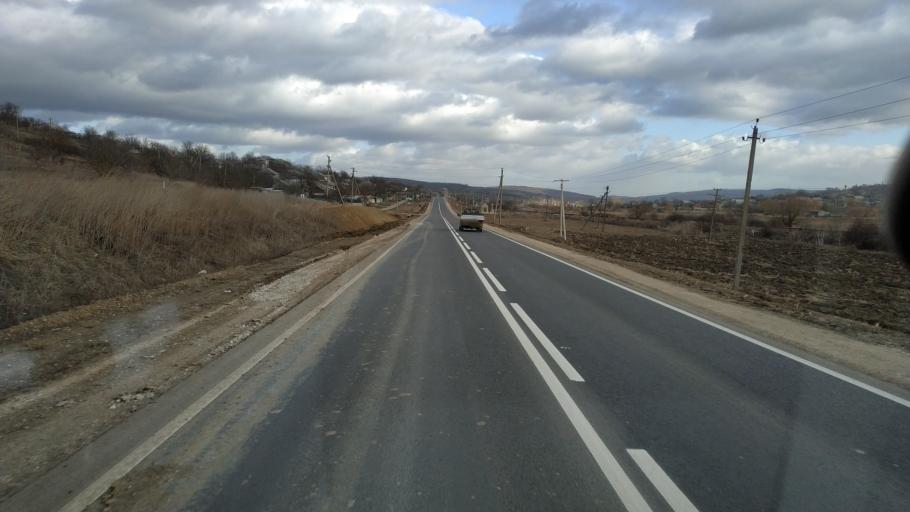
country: MD
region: Calarasi
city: Calarasi
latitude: 47.2915
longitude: 28.1792
